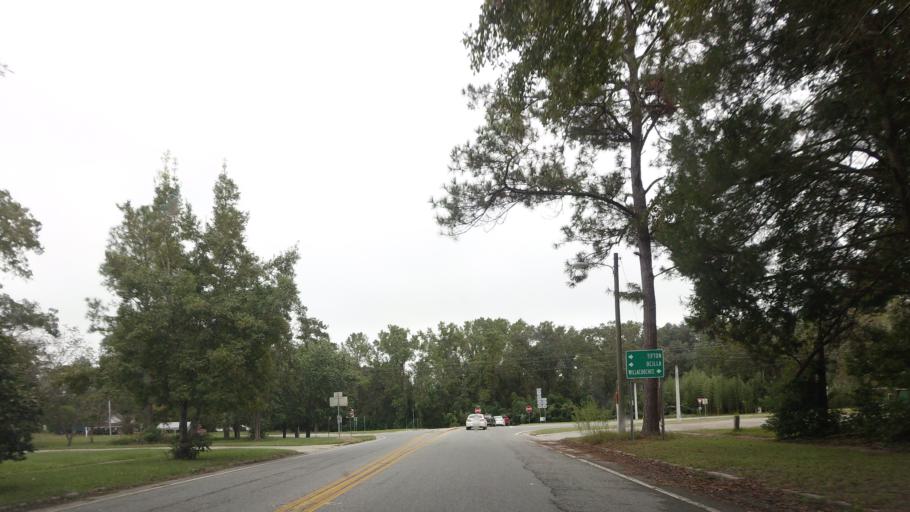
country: US
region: Georgia
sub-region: Berrien County
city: Enigma
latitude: 31.3846
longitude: -83.2232
